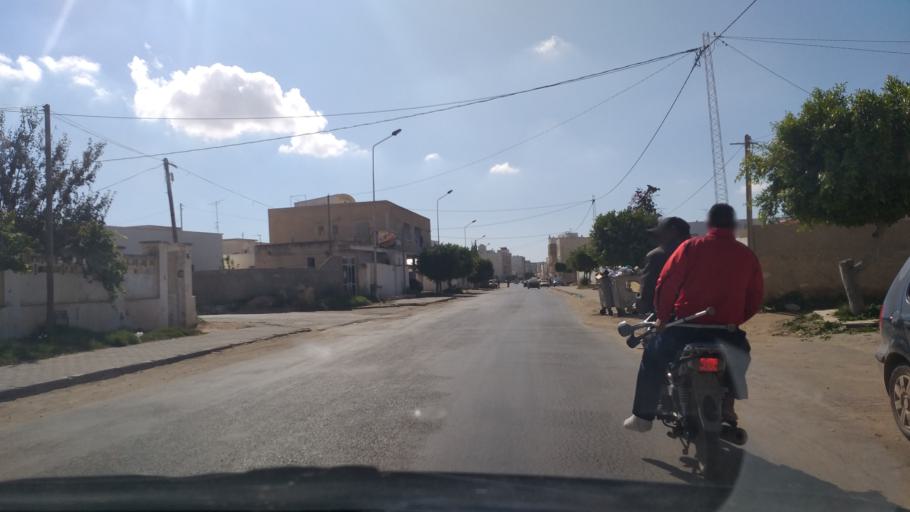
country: TN
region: Safaqis
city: Al Qarmadah
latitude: 34.8019
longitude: 10.7812
